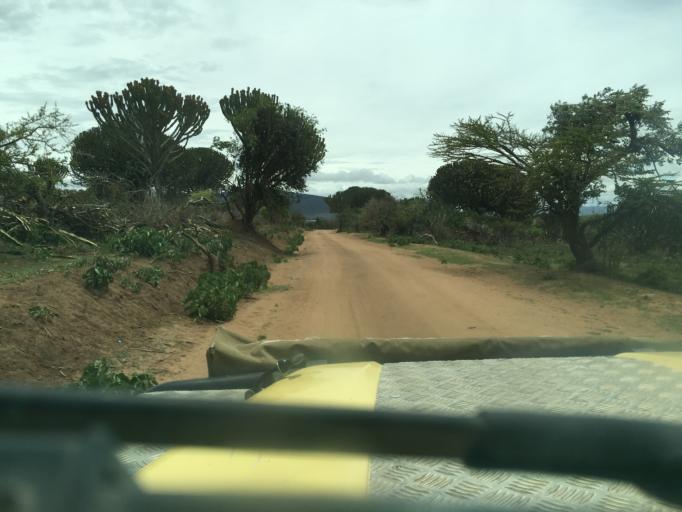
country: KE
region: Kajiado
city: Magadi
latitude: -2.0269
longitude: 35.5337
